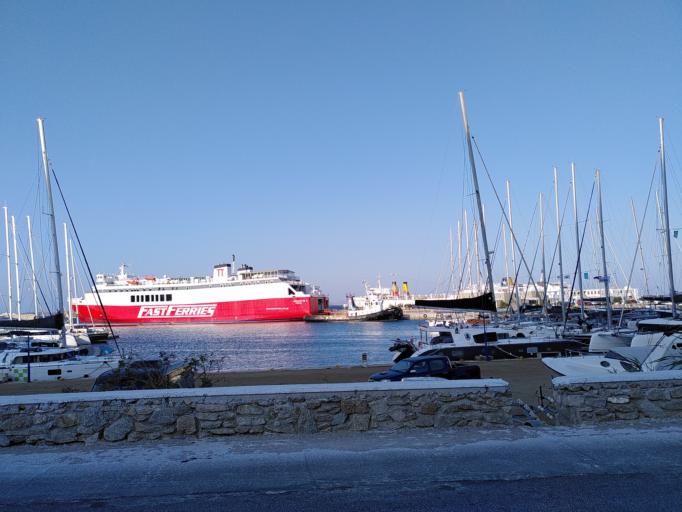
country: GR
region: South Aegean
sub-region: Nomos Kykladon
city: Mykonos
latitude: 37.4643
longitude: 25.3283
